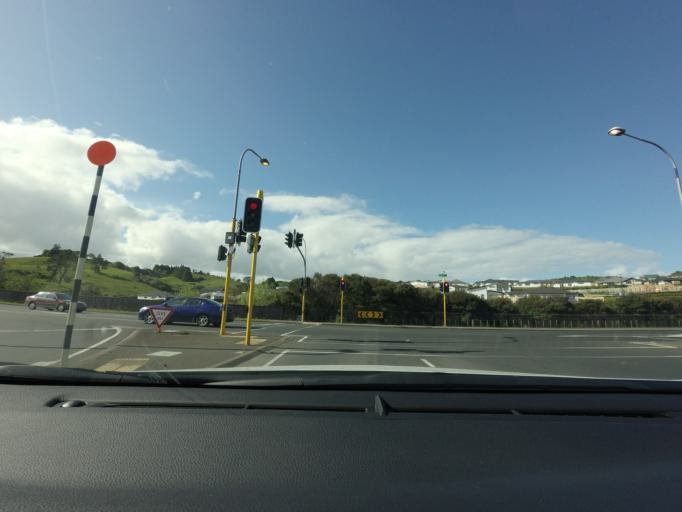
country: NZ
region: Auckland
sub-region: Auckland
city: Rothesay Bay
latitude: -36.5894
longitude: 174.6718
